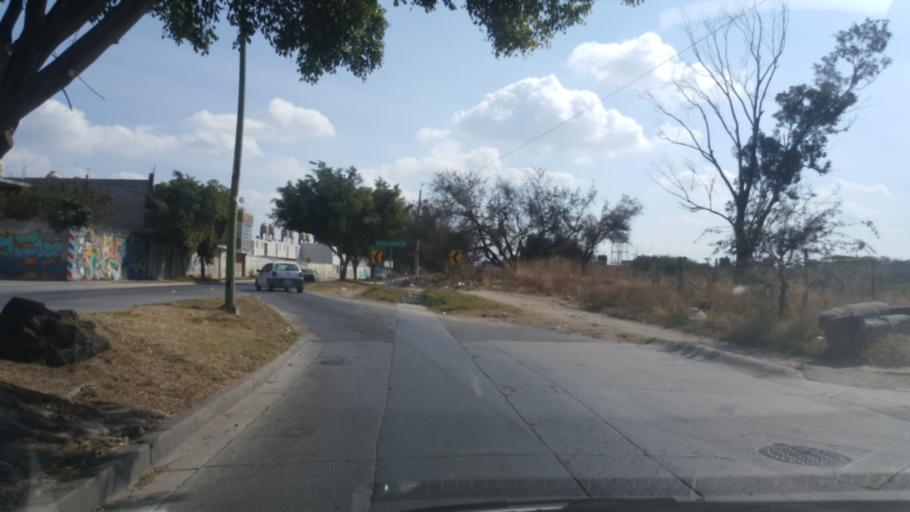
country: MX
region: Guanajuato
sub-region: Leon
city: Fraccionamiento Paraiso Real
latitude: 21.0996
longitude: -101.6094
